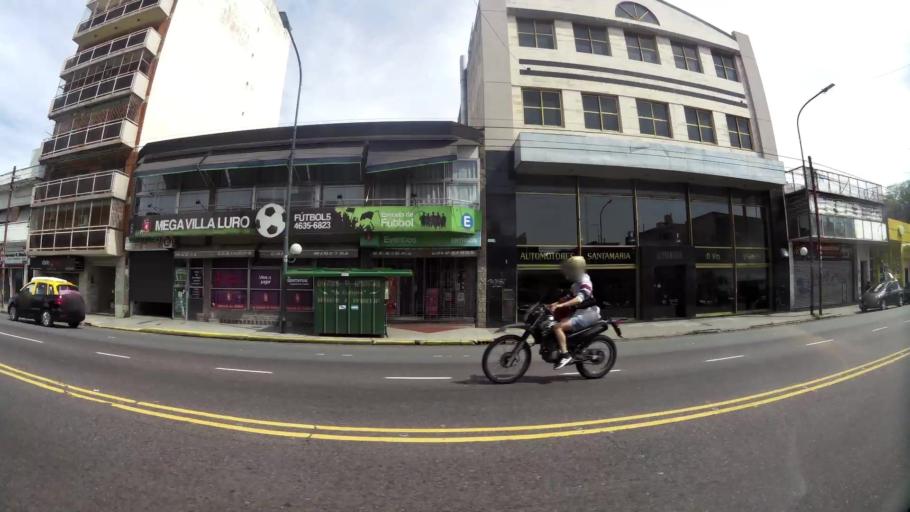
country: AR
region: Buenos Aires F.D.
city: Villa Santa Rita
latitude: -34.6387
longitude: -58.5080
